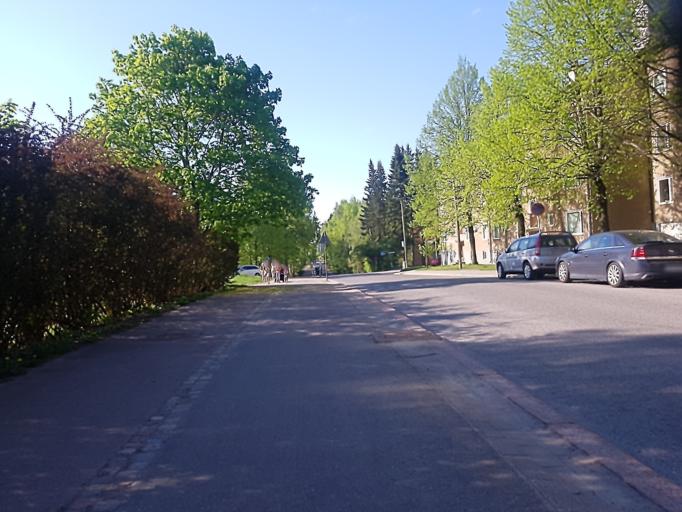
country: FI
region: Uusimaa
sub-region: Helsinki
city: Helsinki
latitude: 60.2276
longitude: 24.9341
